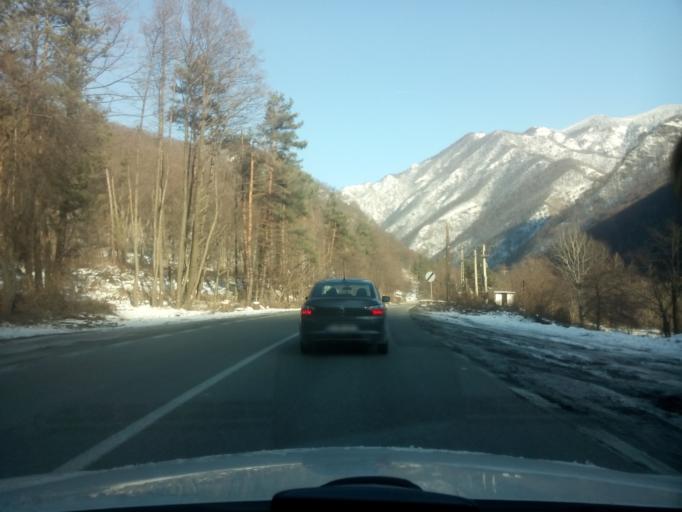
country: RO
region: Valcea
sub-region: Comuna Brezoi
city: Brezoi
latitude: 45.3110
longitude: 24.2693
